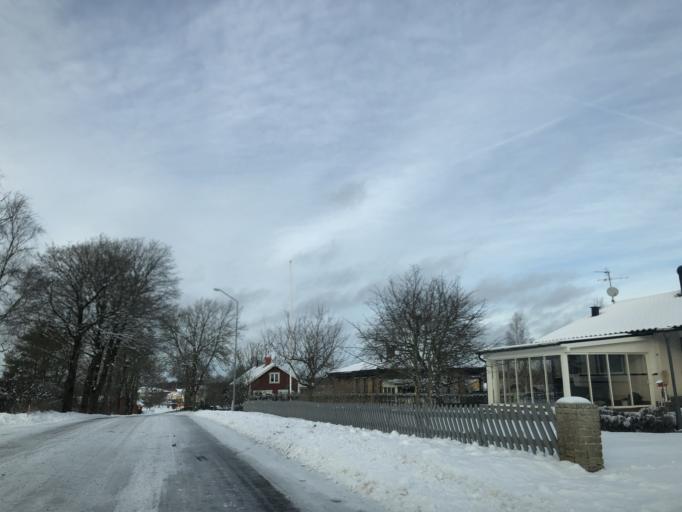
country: SE
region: Vaestra Goetaland
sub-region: Ulricehamns Kommun
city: Ulricehamn
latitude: 57.8181
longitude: 13.5323
